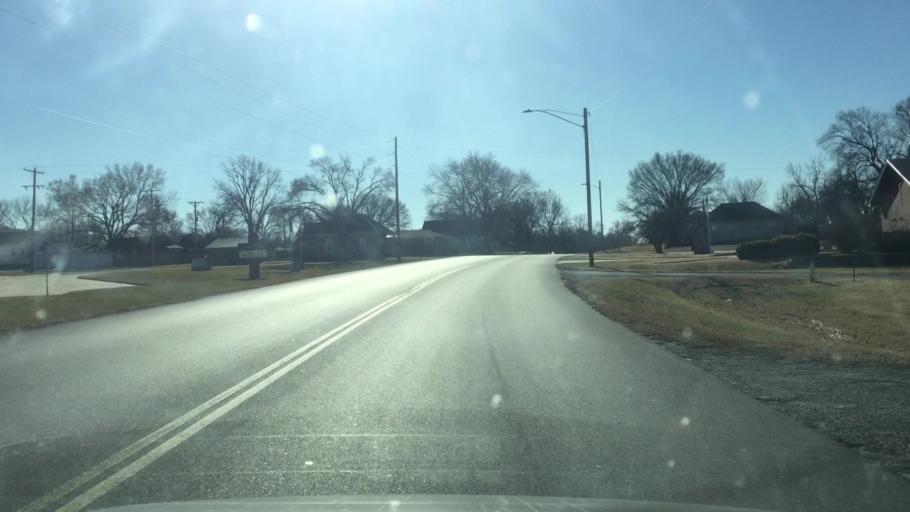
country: US
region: Kansas
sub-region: Allen County
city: Humboldt
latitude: 37.8184
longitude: -95.4358
